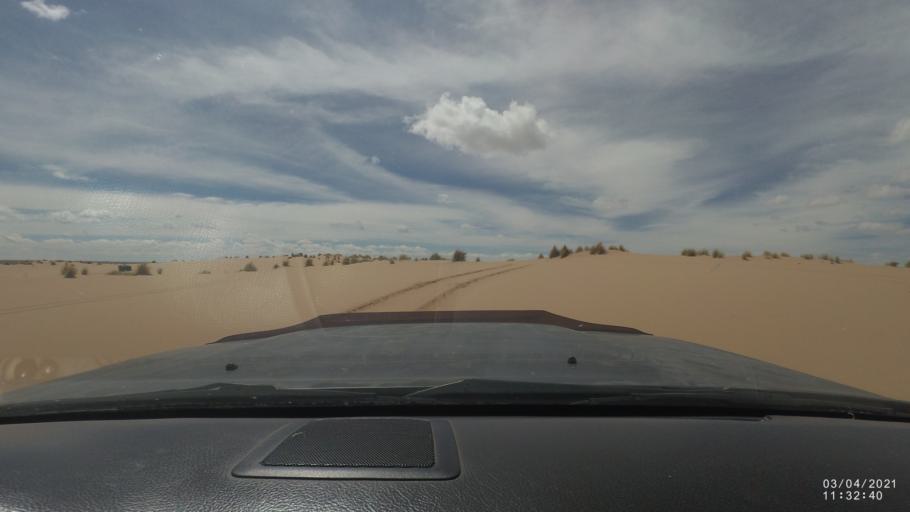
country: BO
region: Oruro
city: Poopo
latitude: -18.7024
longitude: -67.5066
